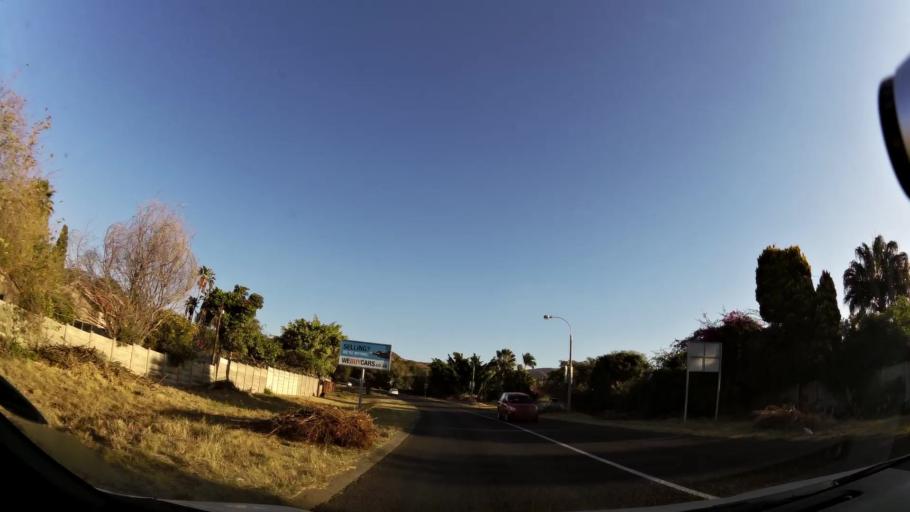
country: ZA
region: North-West
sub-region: Bojanala Platinum District Municipality
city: Rustenburg
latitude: -25.6969
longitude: 27.2190
